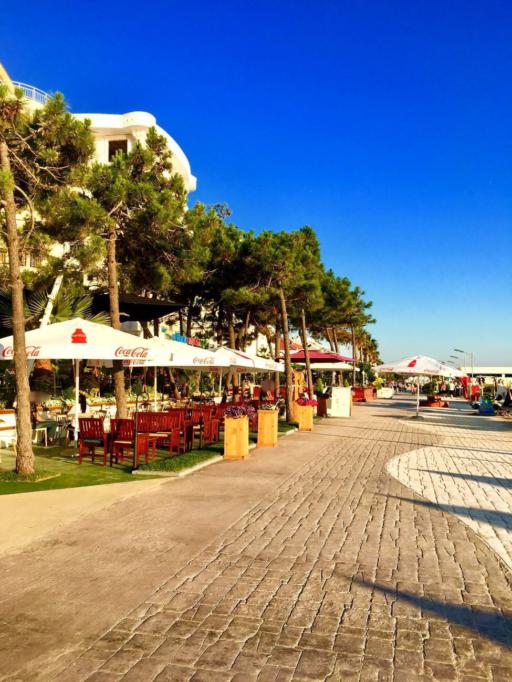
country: AL
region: Tirane
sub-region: Rrethi i Kavajes
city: Golem
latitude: 41.2472
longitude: 19.5169
